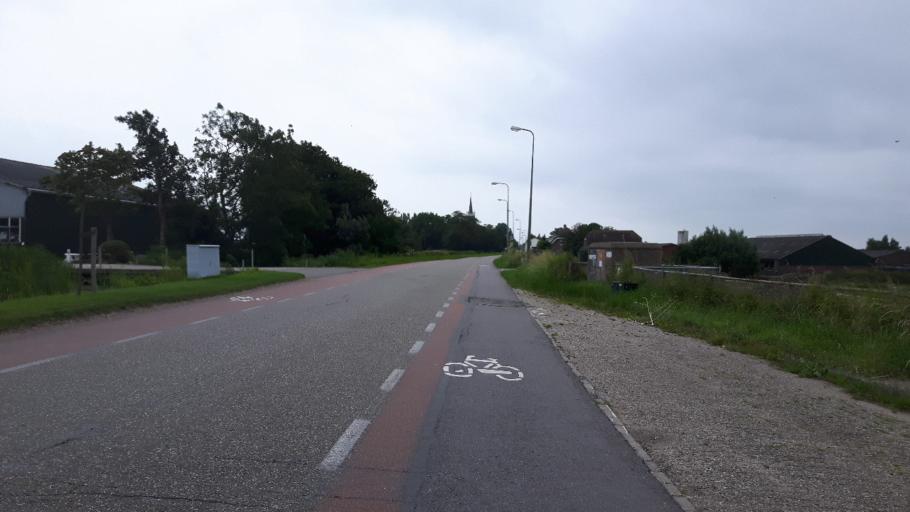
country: NL
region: South Holland
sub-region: Gemeente Kaag en Braassem
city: Leimuiden
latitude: 52.2144
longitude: 4.6699
